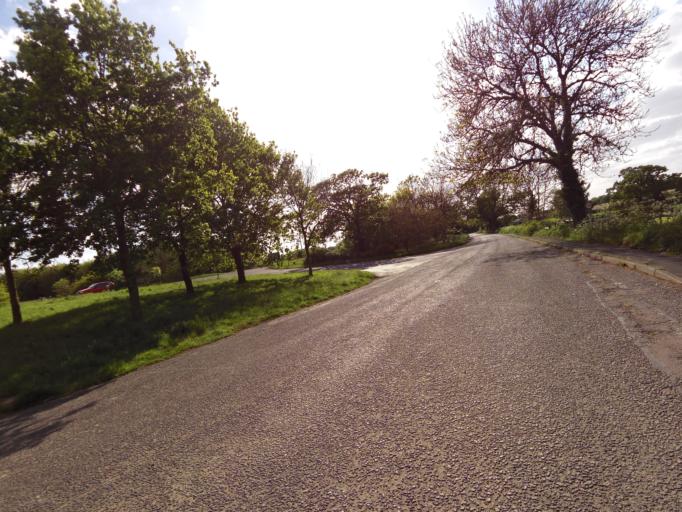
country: GB
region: England
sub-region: Suffolk
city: Beccles
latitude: 52.4467
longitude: 1.6198
